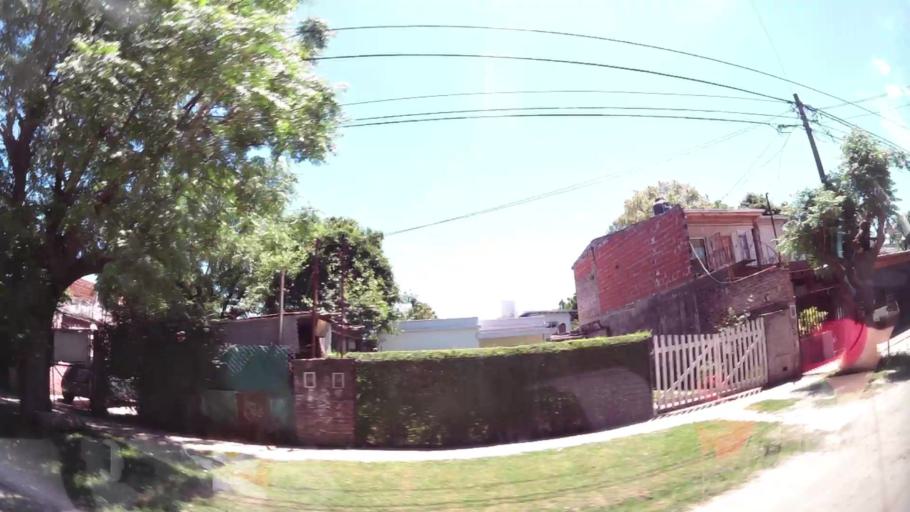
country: AR
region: Buenos Aires
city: Hurlingham
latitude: -34.5069
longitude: -58.7161
